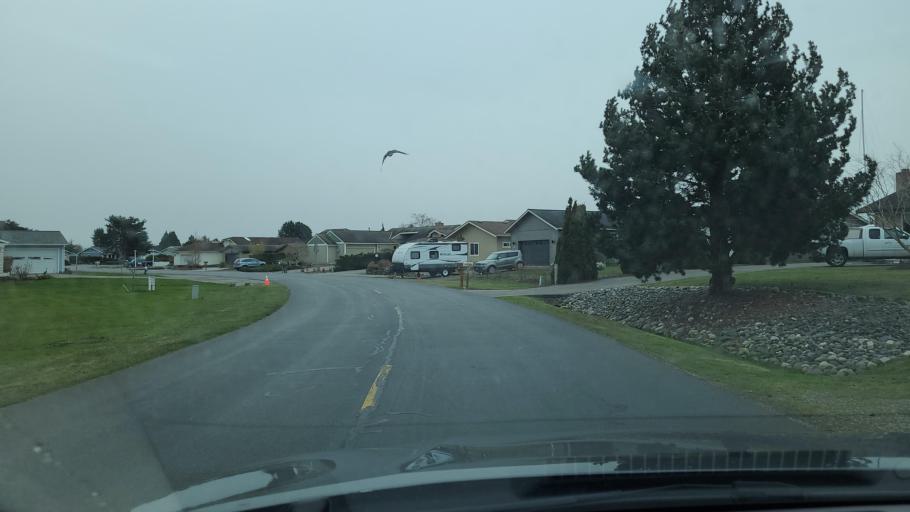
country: US
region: Washington
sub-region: Whatcom County
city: Birch Bay
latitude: 48.9417
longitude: -122.7865
